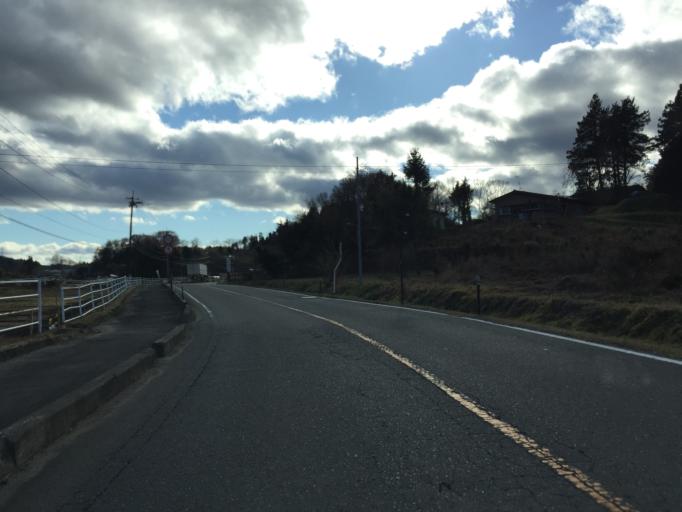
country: JP
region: Fukushima
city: Funehikimachi-funehiki
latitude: 37.5899
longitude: 140.5775
